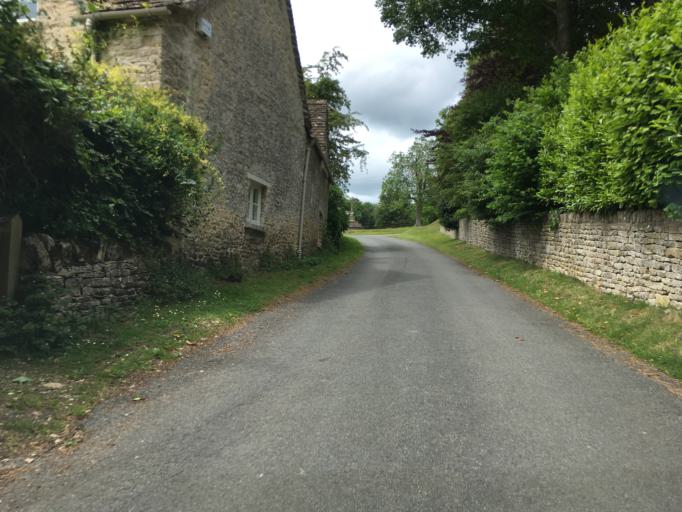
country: GB
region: England
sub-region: Gloucestershire
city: Cirencester
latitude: 51.7589
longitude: -1.9858
